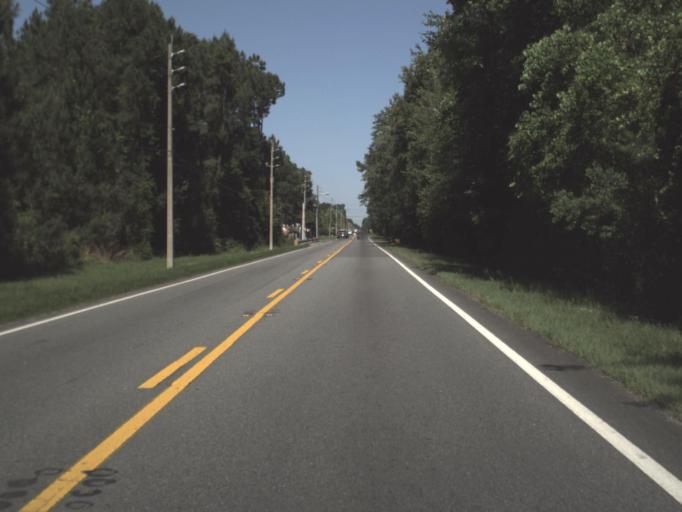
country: US
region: Florida
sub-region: Duval County
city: Baldwin
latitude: 30.3164
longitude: -81.8296
